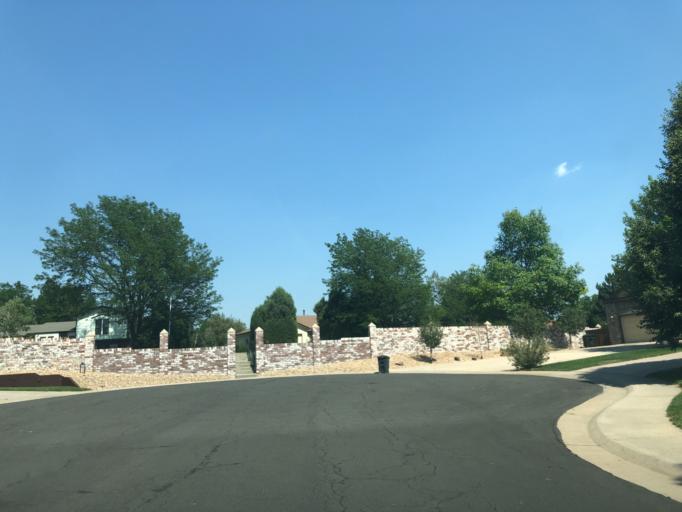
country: US
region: Colorado
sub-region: Arapahoe County
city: Dove Valley
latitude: 39.6355
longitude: -104.7713
